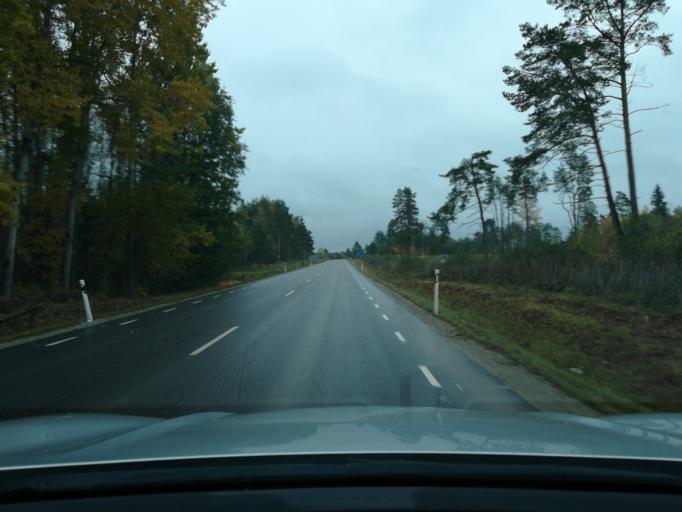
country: EE
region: Ida-Virumaa
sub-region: Johvi vald
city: Johvi
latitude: 59.2964
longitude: 27.4857
